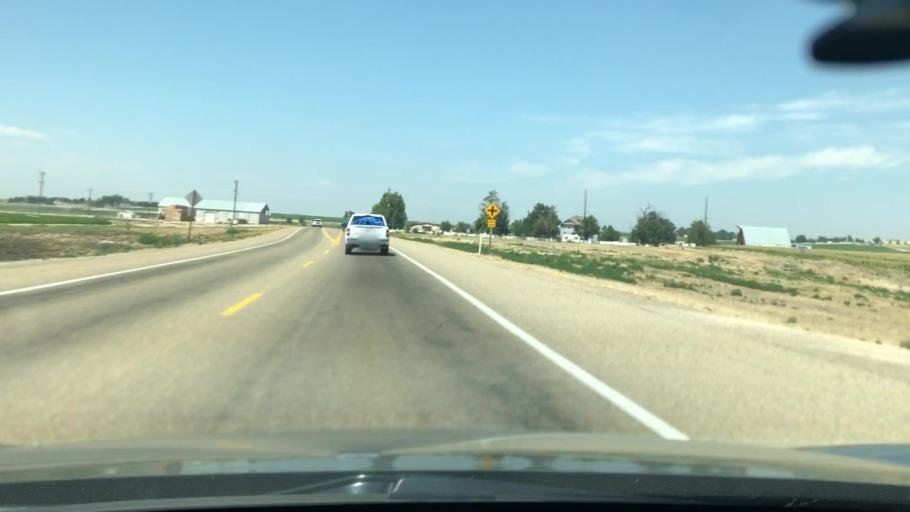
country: US
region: Idaho
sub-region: Canyon County
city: Parma
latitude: 43.8048
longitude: -116.9527
